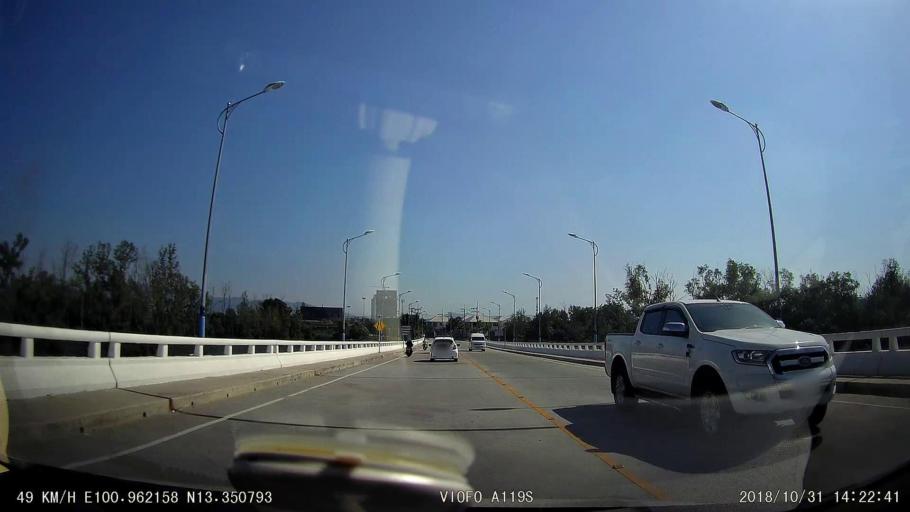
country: TH
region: Chon Buri
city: Chon Buri
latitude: 13.3505
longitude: 100.9622
